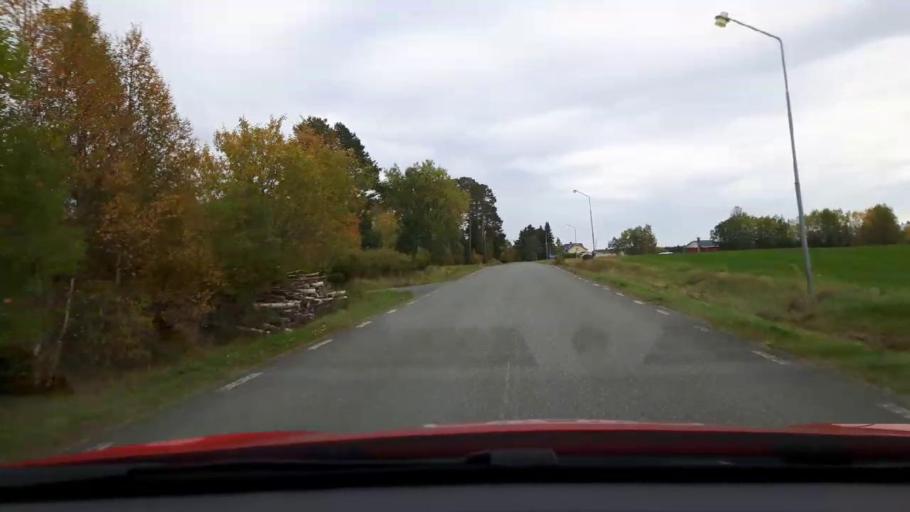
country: SE
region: Jaemtland
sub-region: Krokoms Kommun
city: Krokom
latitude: 63.2277
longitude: 14.1311
